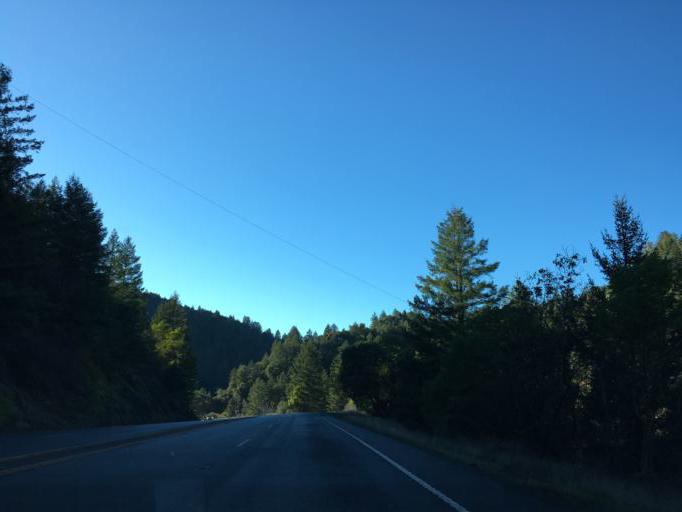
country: US
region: California
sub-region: Mendocino County
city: Laytonville
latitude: 39.8292
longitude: -123.6018
